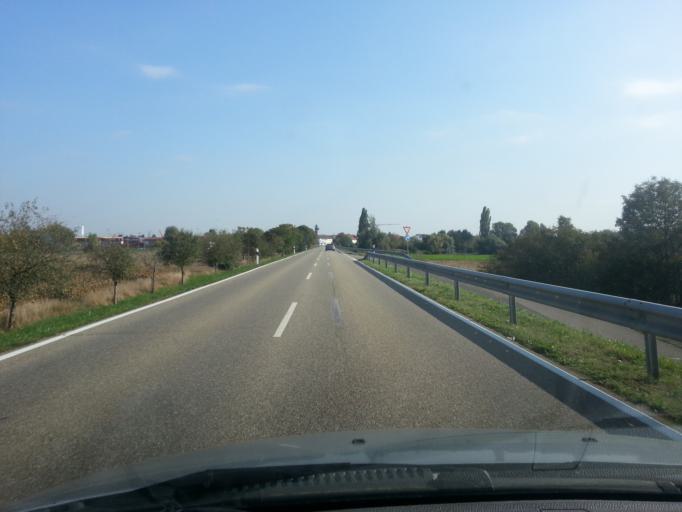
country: DE
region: Baden-Wuerttemberg
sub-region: Karlsruhe Region
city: Altlussheim
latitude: 49.3076
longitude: 8.4888
